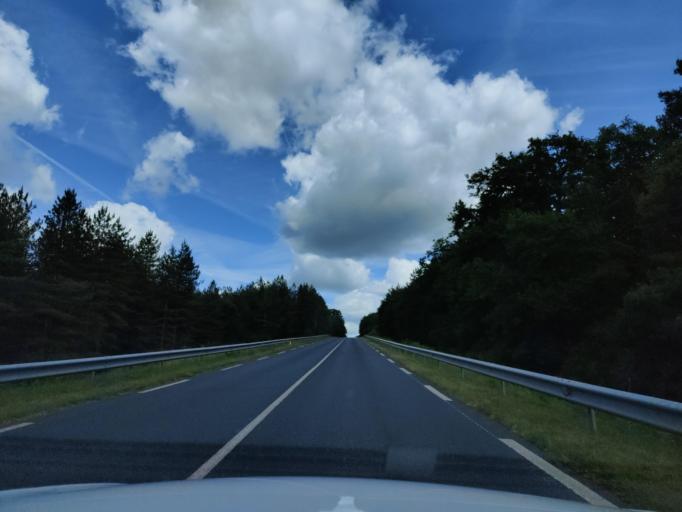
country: FR
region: Auvergne
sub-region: Departement de l'Allier
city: Vallon-en-Sully
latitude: 46.5620
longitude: 2.6220
